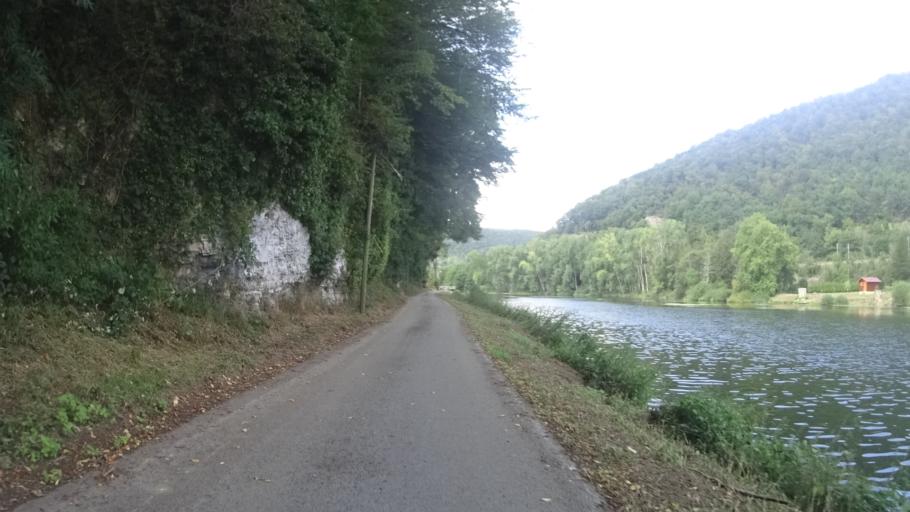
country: FR
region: Franche-Comte
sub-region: Departement du Doubs
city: Clerval
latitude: 47.3649
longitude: 6.4421
